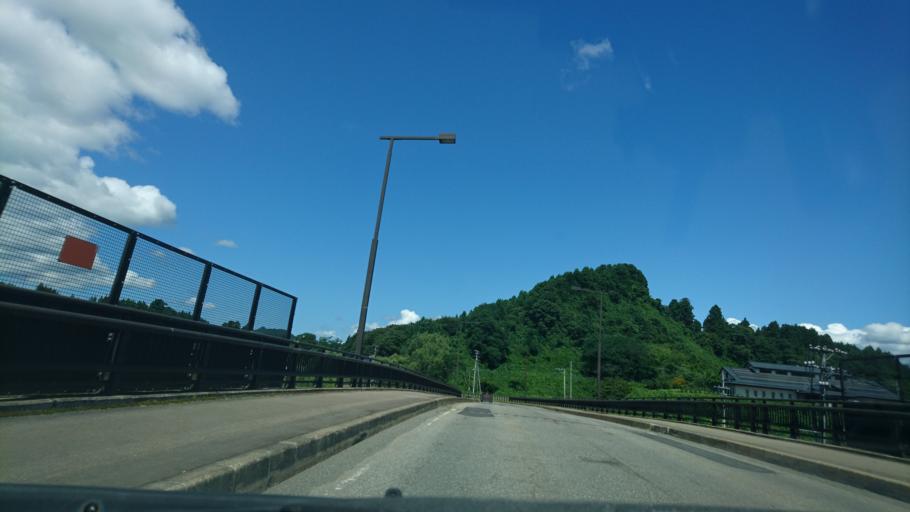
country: JP
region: Akita
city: Kakunodatemachi
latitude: 39.5878
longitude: 140.5690
